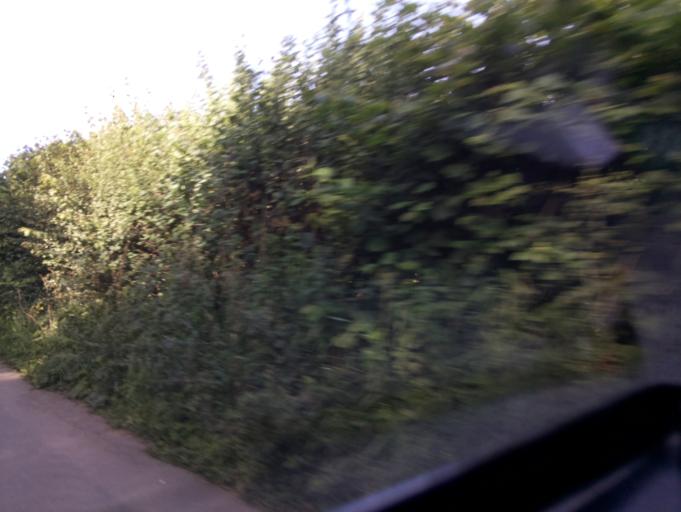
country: GB
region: England
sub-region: South Gloucestershire
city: Bitton
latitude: 51.4342
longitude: -2.4507
